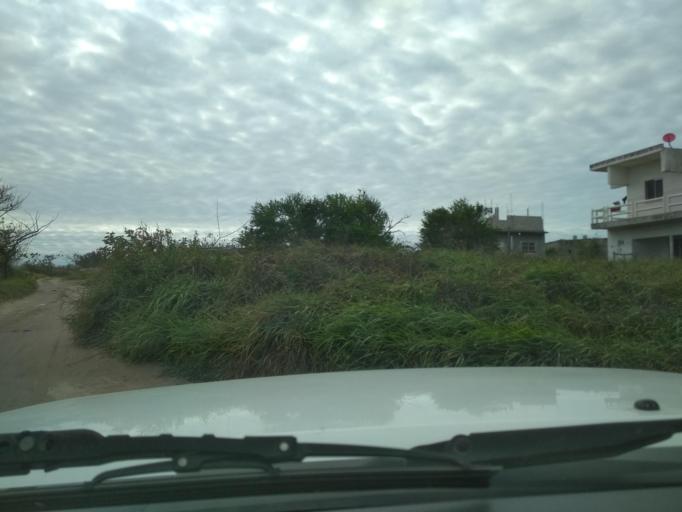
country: MX
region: Veracruz
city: Anton Lizardo
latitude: 19.0525
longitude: -95.9867
